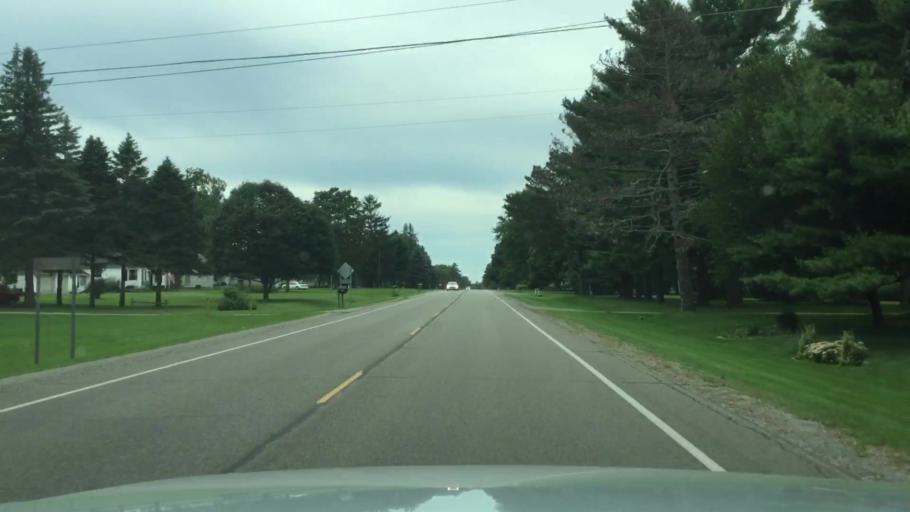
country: US
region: Michigan
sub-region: Shiawassee County
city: Durand
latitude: 42.9327
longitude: -83.9503
